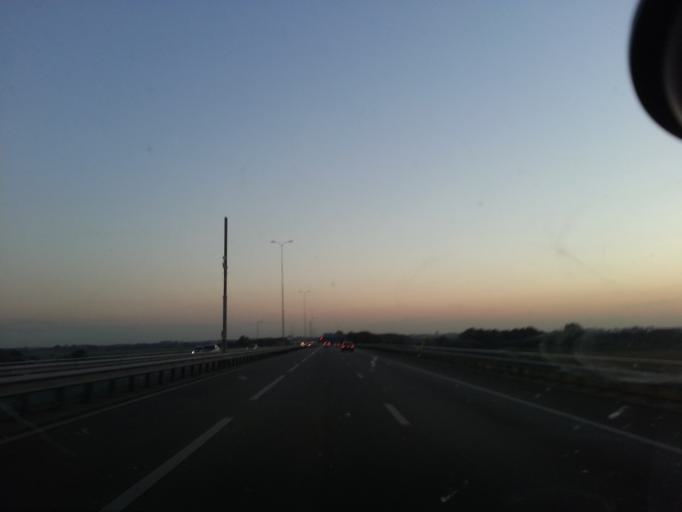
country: NL
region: Utrecht
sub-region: Gemeente Vianen
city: Vianen
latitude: 52.0007
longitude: 5.1141
